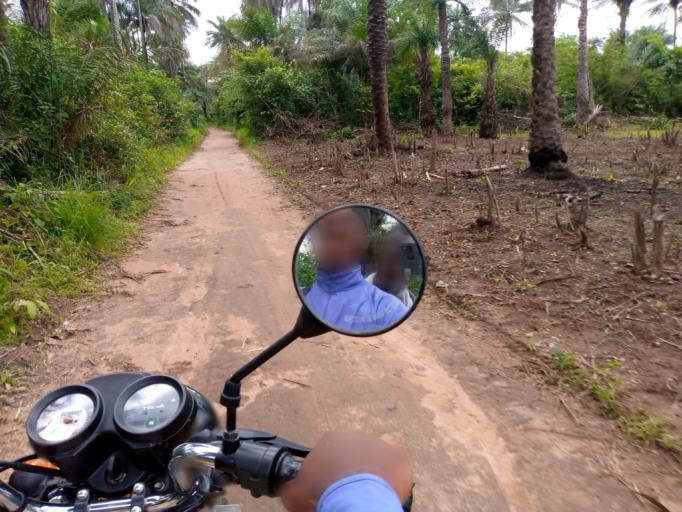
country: SL
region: Northern Province
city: Mange
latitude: 8.9823
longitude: -12.8192
